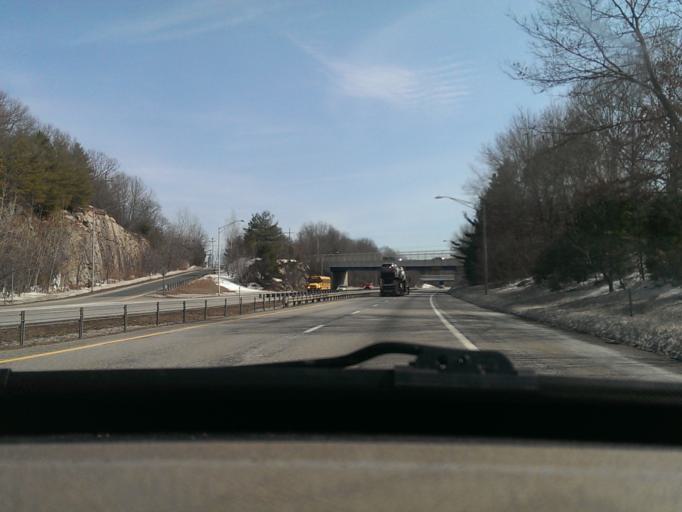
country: US
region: Massachusetts
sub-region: Worcester County
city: Blackstone
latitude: 42.0033
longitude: -71.5622
